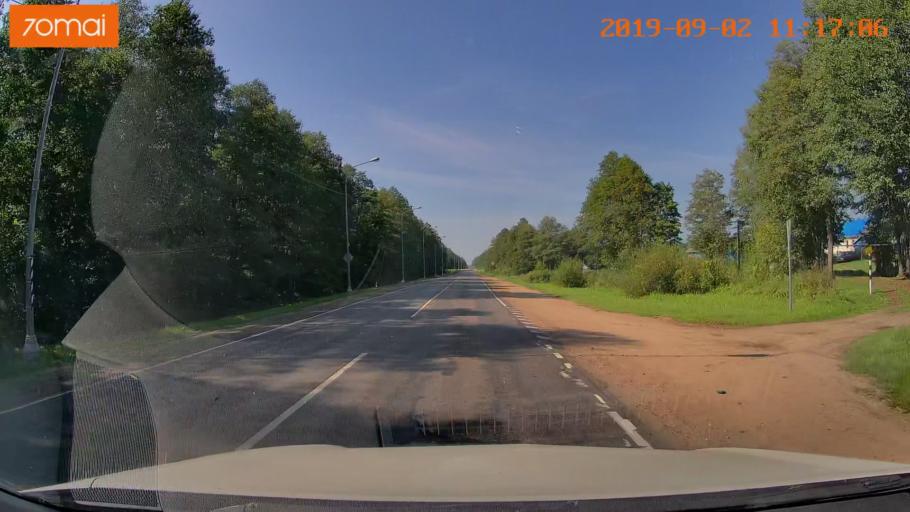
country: RU
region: Smolensk
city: Yekimovichi
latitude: 54.0639
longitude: 33.1256
